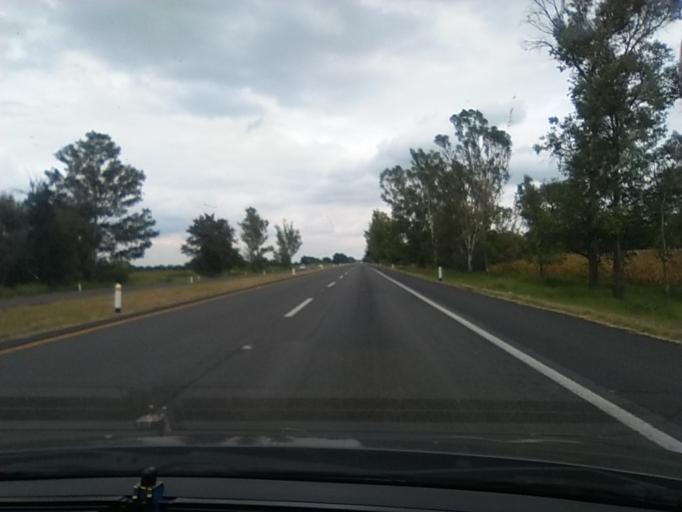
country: MX
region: Jalisco
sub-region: Ocotlan
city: Joconoxtle (La Tuna)
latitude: 20.3792
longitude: -102.6891
